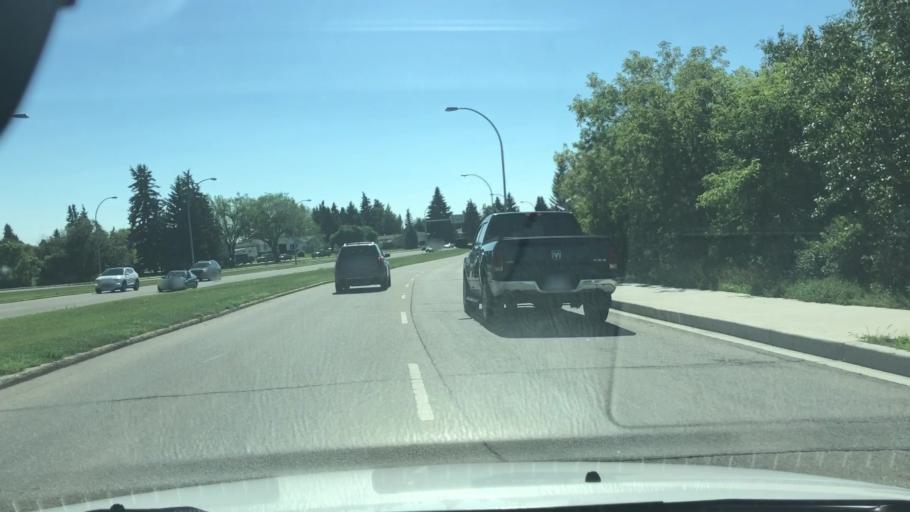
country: CA
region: Alberta
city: Edmonton
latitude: 53.5384
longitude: -113.4304
